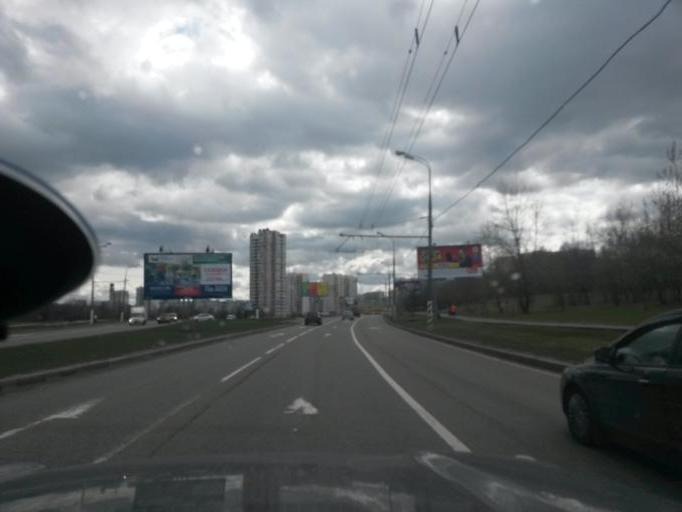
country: RU
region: Moscow
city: Yasenevo
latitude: 55.6235
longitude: 37.5424
